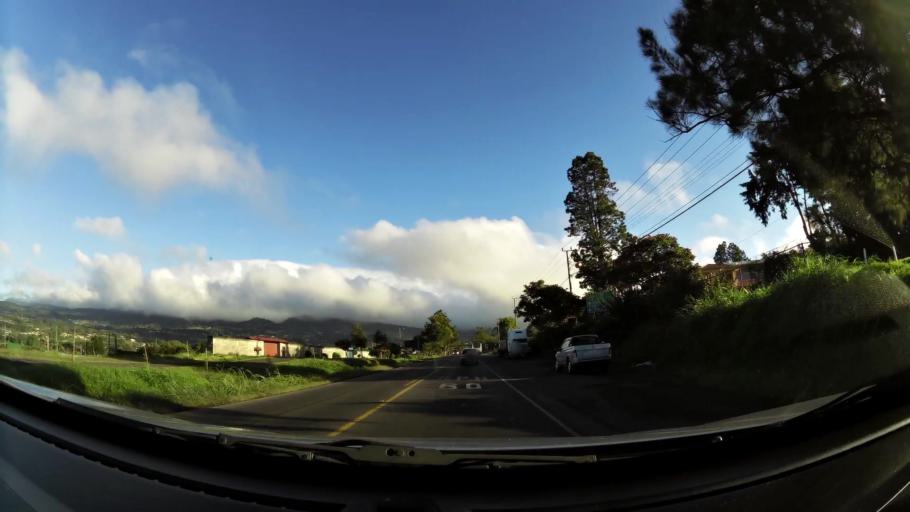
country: CR
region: Heredia
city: Angeles
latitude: 10.0057
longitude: -84.0325
